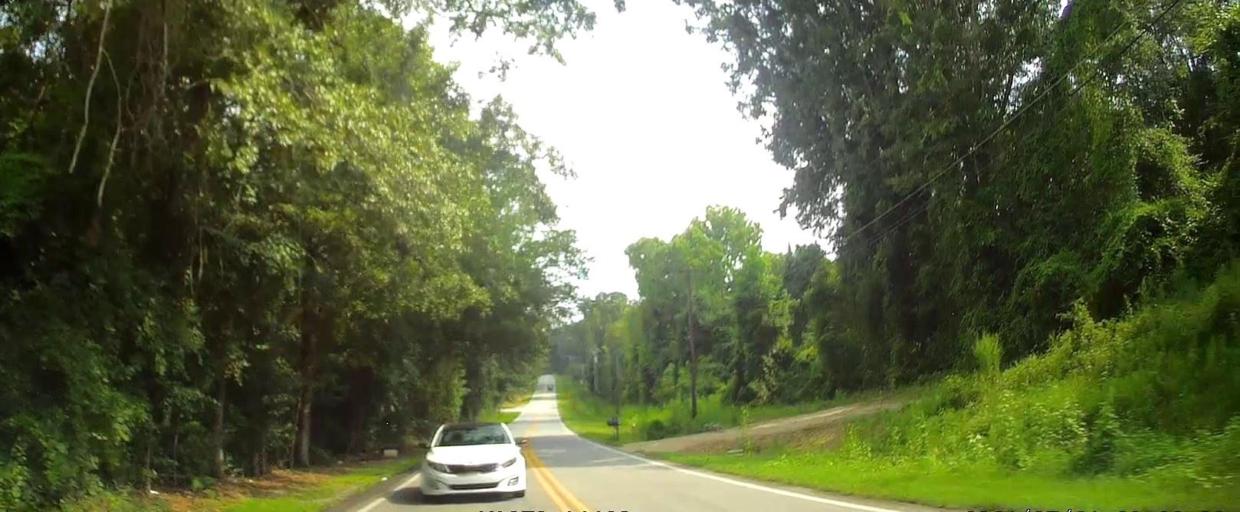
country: US
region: Georgia
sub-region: Houston County
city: Robins Air Force Base
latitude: 32.5736
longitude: -83.6096
